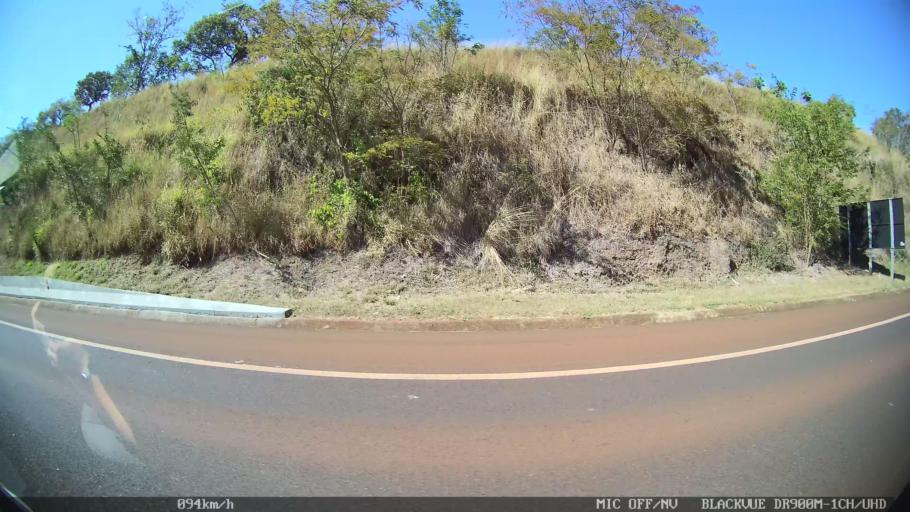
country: BR
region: Sao Paulo
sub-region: Franca
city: Franca
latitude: -20.6238
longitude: -47.4615
